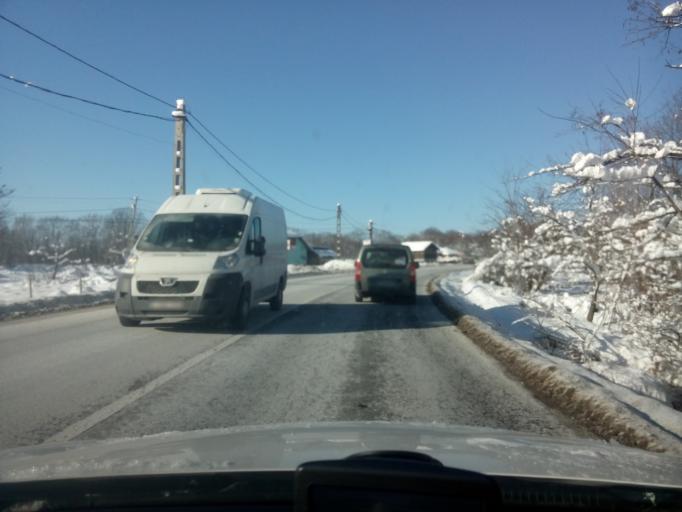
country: RO
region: Arges
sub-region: Comuna Cotmeana
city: Cotmeana
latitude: 44.9990
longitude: 24.6161
